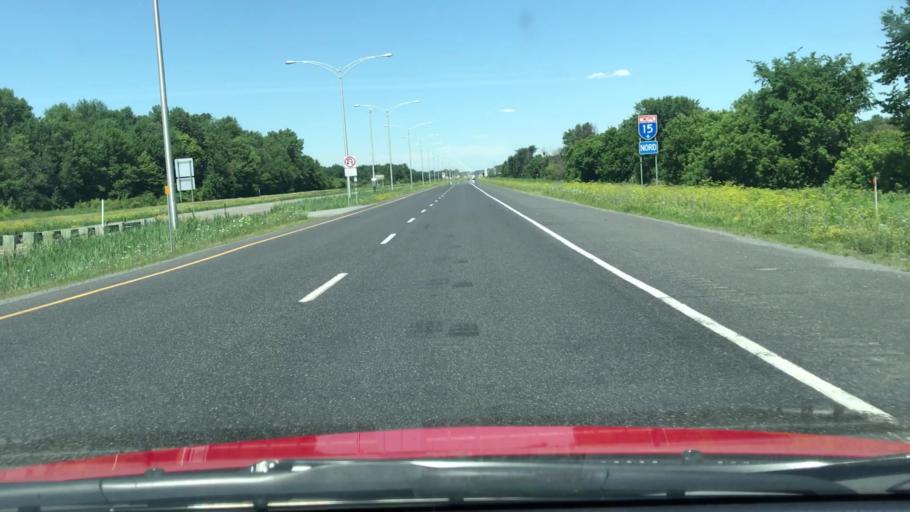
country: US
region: New York
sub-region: Clinton County
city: Champlain
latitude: 45.0230
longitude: -73.4529
